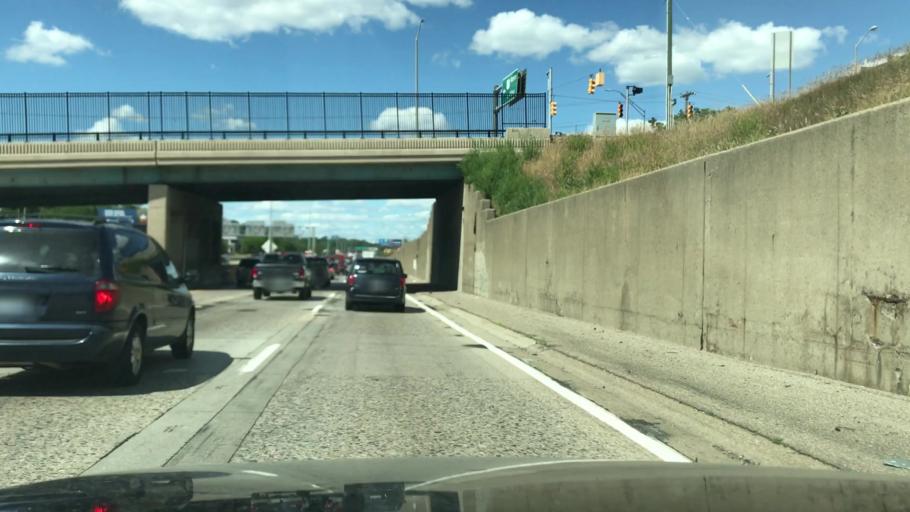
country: US
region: Michigan
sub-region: Kent County
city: Wyoming
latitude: 42.9274
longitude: -85.6817
